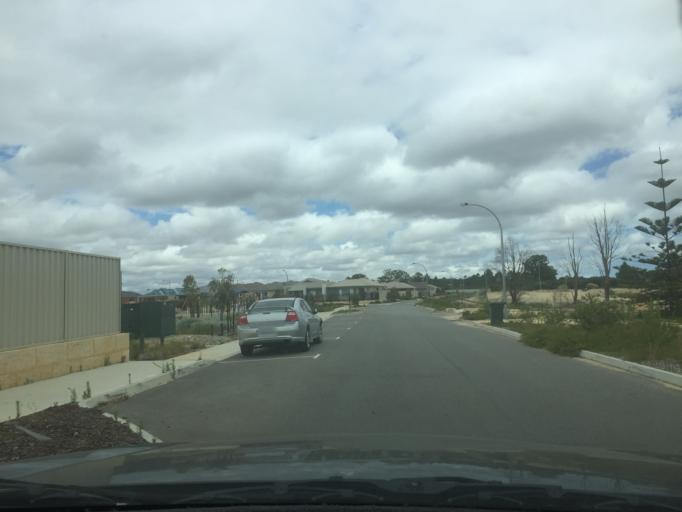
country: AU
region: Western Australia
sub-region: Armadale
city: Harrisdale
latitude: -32.1371
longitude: 115.9062
